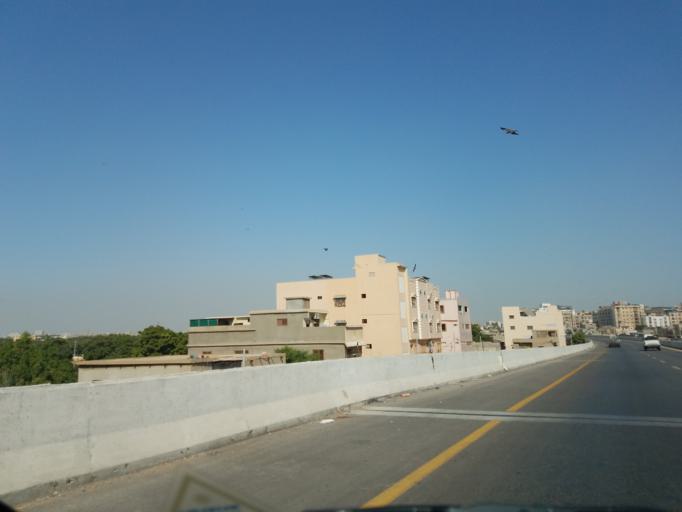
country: PK
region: Sindh
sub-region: Karachi District
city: Karachi
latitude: 24.8796
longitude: 67.0133
